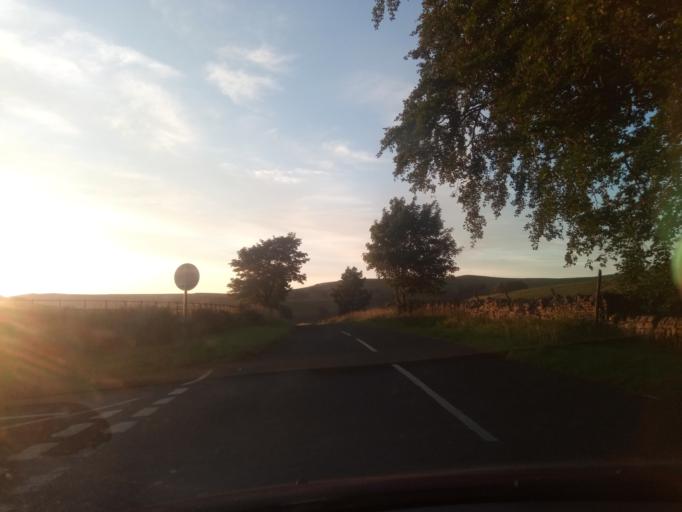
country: GB
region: England
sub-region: Northumberland
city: Bardon Mill
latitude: 54.8082
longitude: -2.3850
